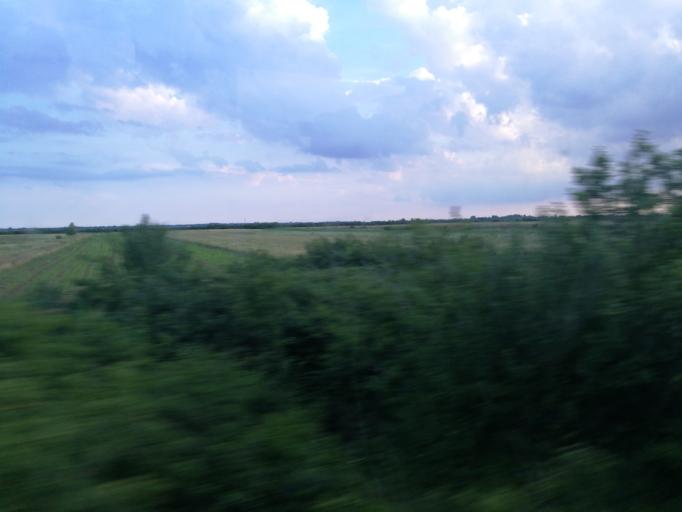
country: RO
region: Dambovita
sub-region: Comuna Produlesti
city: Costestii din Deal
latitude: 44.6788
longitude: 25.4788
